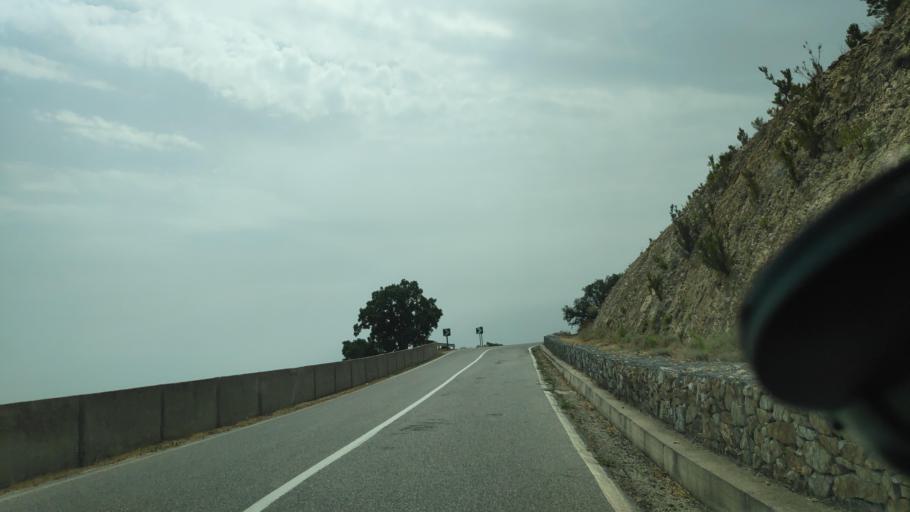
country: IT
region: Calabria
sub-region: Provincia di Catanzaro
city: San Sostene
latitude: 38.6379
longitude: 16.5112
